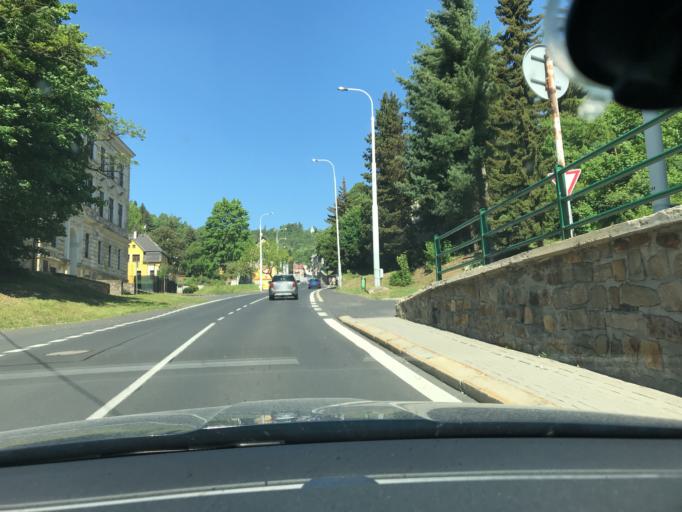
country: CZ
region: Karlovarsky
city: Jachymov
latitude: 50.3634
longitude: 12.9262
